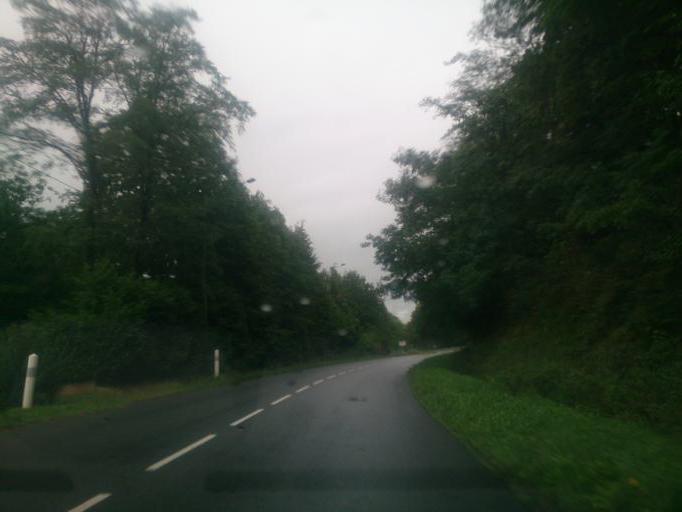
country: FR
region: Limousin
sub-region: Departement de la Correze
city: Malemort-sur-Correze
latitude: 45.1810
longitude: 1.5727
